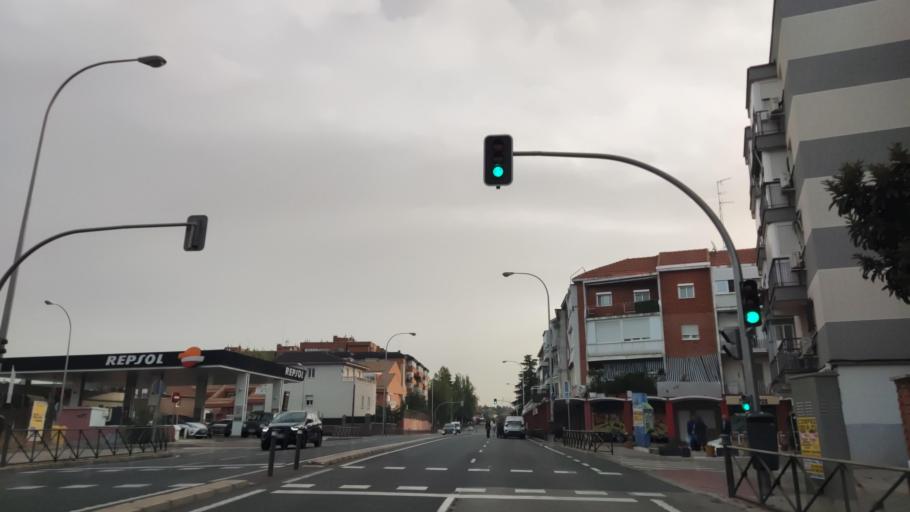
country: ES
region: Madrid
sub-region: Provincia de Madrid
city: Tetuan de las Victorias
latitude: 40.4787
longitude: -3.7264
